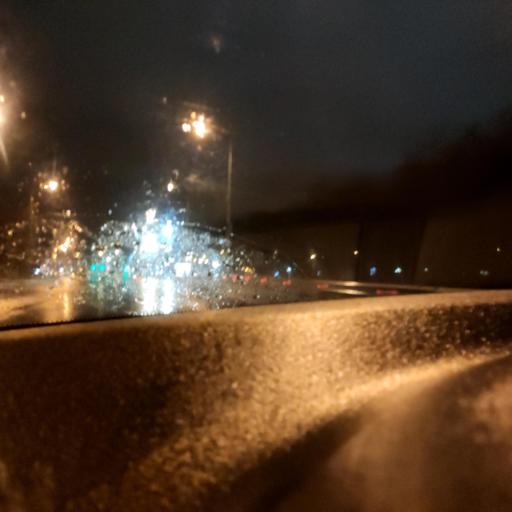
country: RU
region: Samara
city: Petra-Dubrava
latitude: 53.2816
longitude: 50.2520
